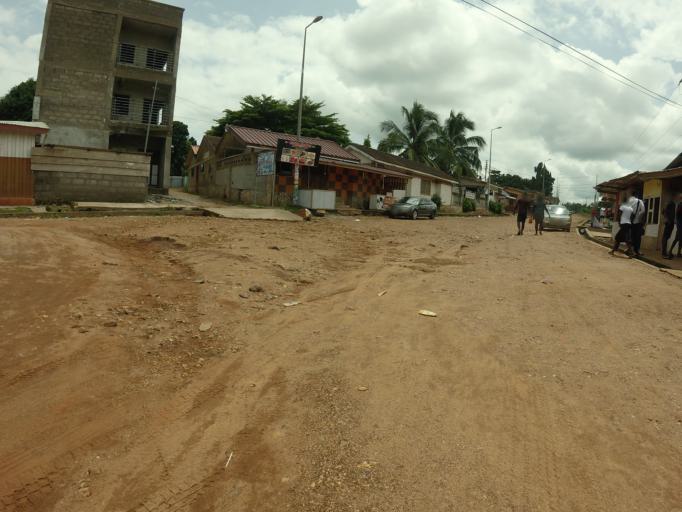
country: GH
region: Volta
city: Ho
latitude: 6.5931
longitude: 0.4708
